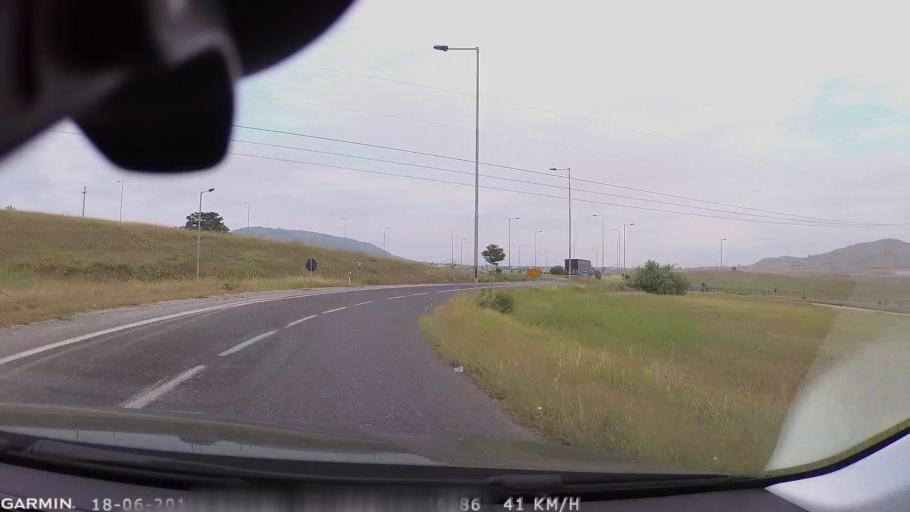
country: MK
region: Stip
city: Shtip
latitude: 41.7635
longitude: 22.1606
